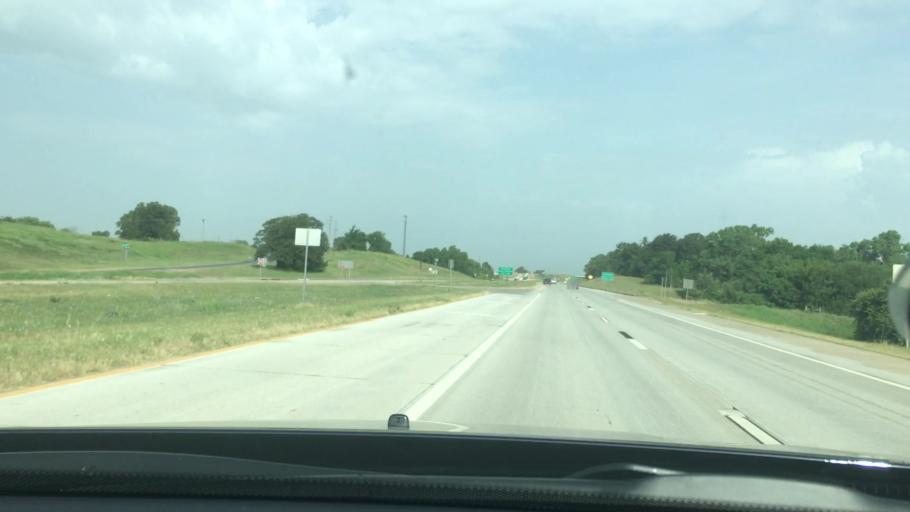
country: US
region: Oklahoma
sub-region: Pontotoc County
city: Ada
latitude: 34.7814
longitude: -96.7151
